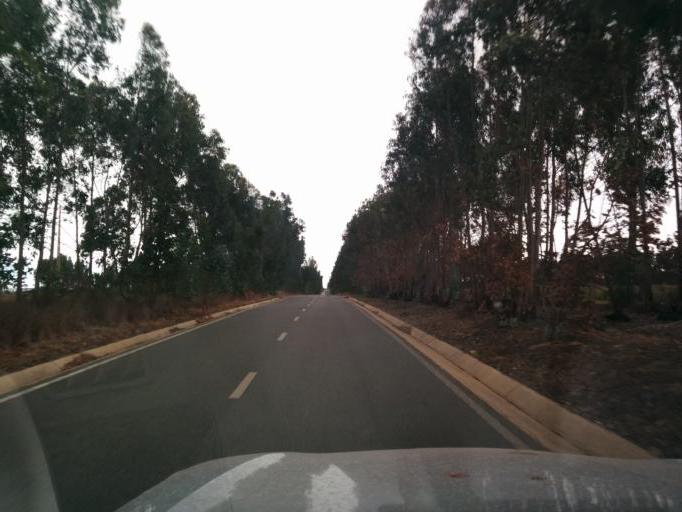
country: PT
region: Beja
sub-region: Odemira
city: Sao Teotonio
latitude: 37.5358
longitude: -8.7538
